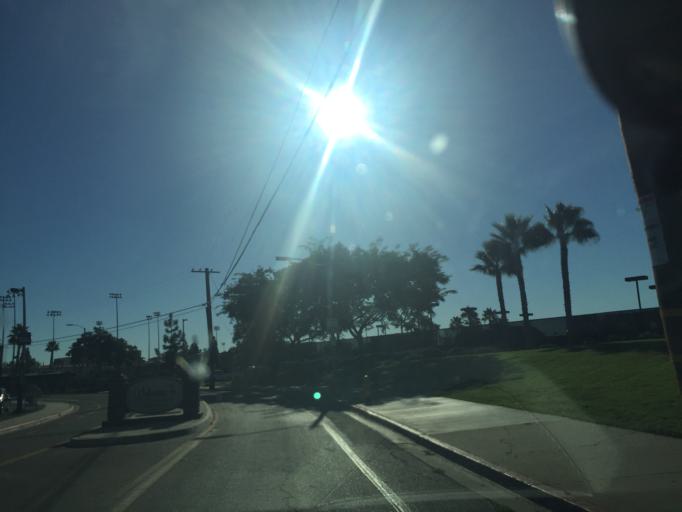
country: US
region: California
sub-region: San Diego County
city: La Mesa
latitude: 32.7754
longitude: -117.0808
